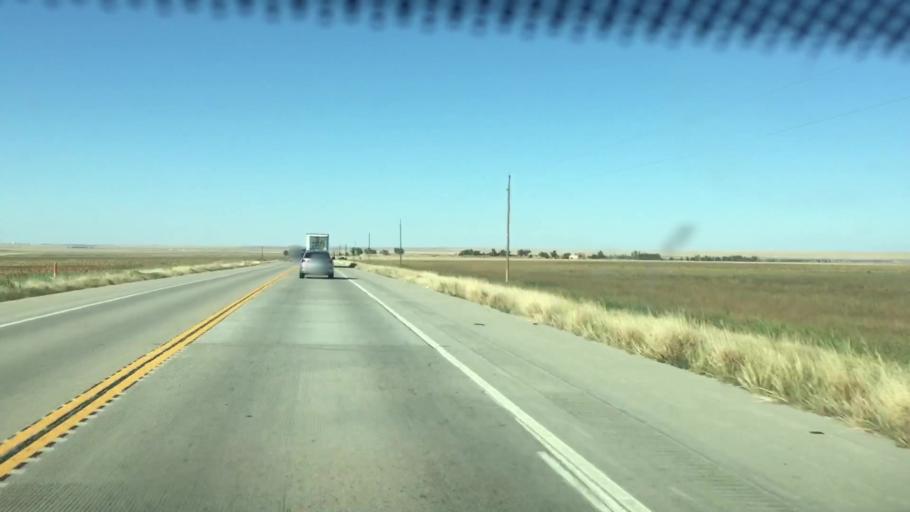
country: US
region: Colorado
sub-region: Kiowa County
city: Eads
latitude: 38.3198
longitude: -102.7196
